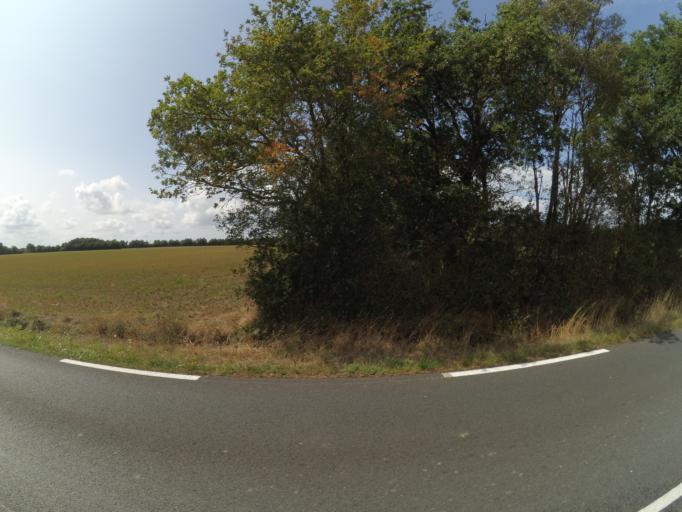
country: FR
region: Pays de la Loire
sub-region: Departement de la Vendee
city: Montaigu
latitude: 47.0079
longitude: -1.2825
